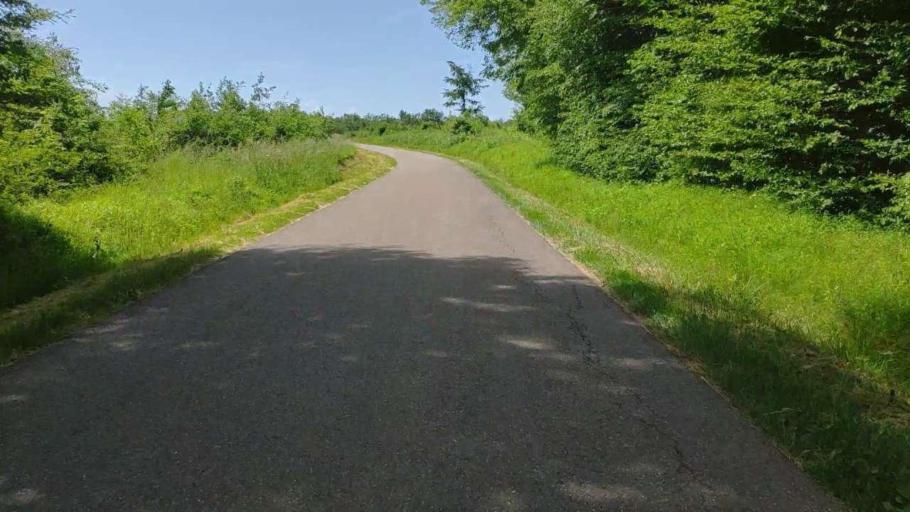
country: FR
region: Franche-Comte
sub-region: Departement du Jura
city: Bletterans
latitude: 46.7101
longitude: 5.4091
